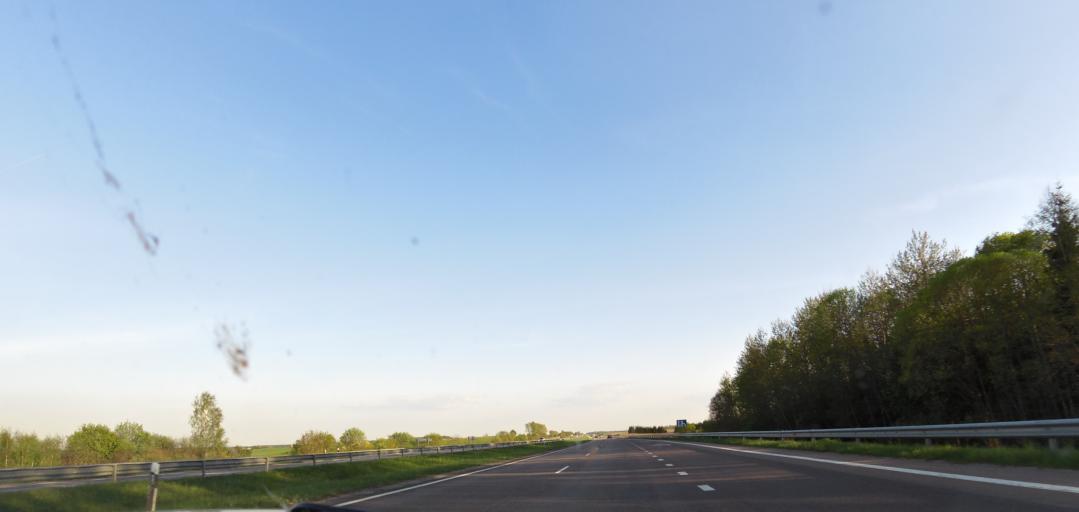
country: LT
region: Vilnius County
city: Ukmerge
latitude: 55.1773
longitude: 24.8117
